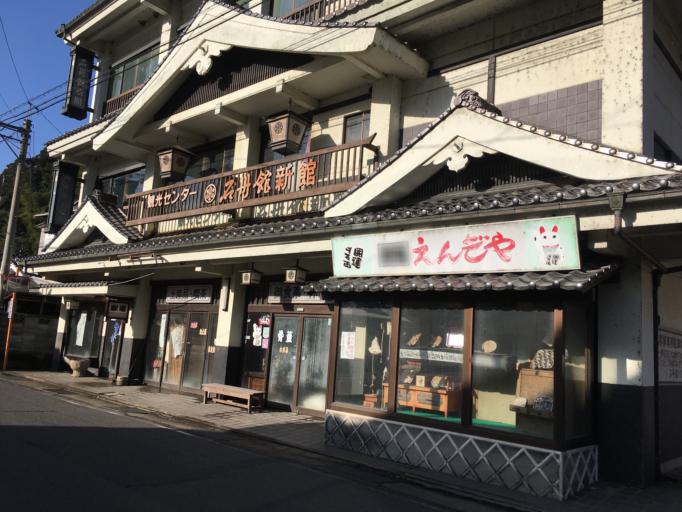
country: JP
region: Shimane
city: Masuda
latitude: 34.4685
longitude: 131.7728
